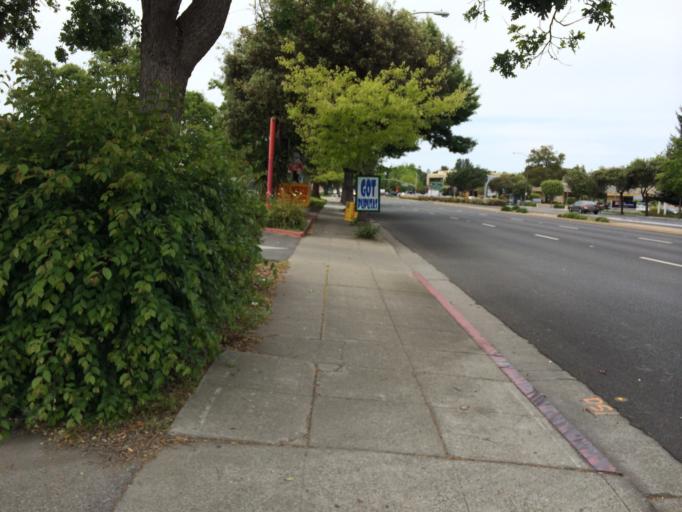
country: US
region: California
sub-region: Santa Clara County
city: Mountain View
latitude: 37.3756
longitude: -122.0612
